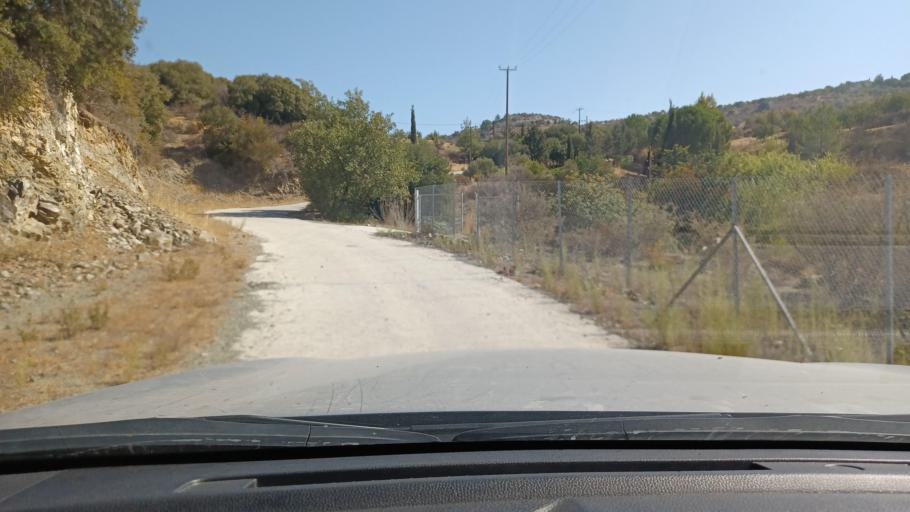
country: CY
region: Pafos
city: Polis
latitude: 35.0005
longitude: 32.4959
